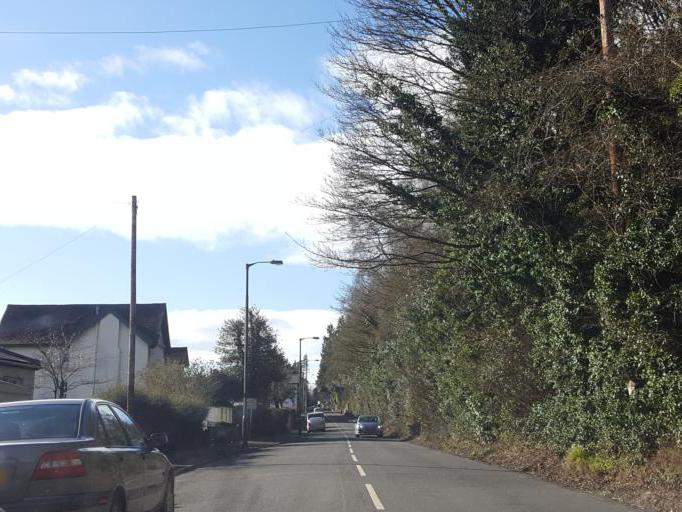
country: GB
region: England
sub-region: Worcestershire
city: Great Malvern
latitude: 52.0805
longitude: -2.3323
